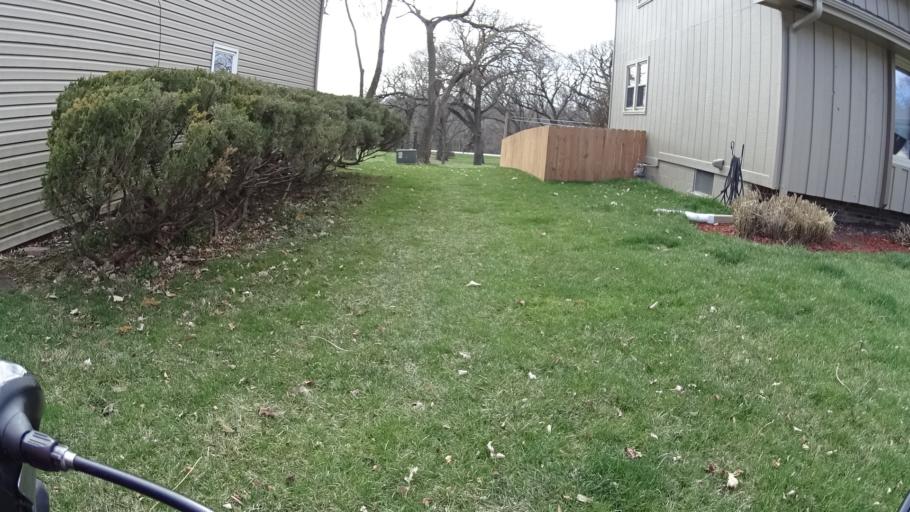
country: US
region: Nebraska
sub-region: Sarpy County
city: Offutt Air Force Base
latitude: 41.1172
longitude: -95.9644
